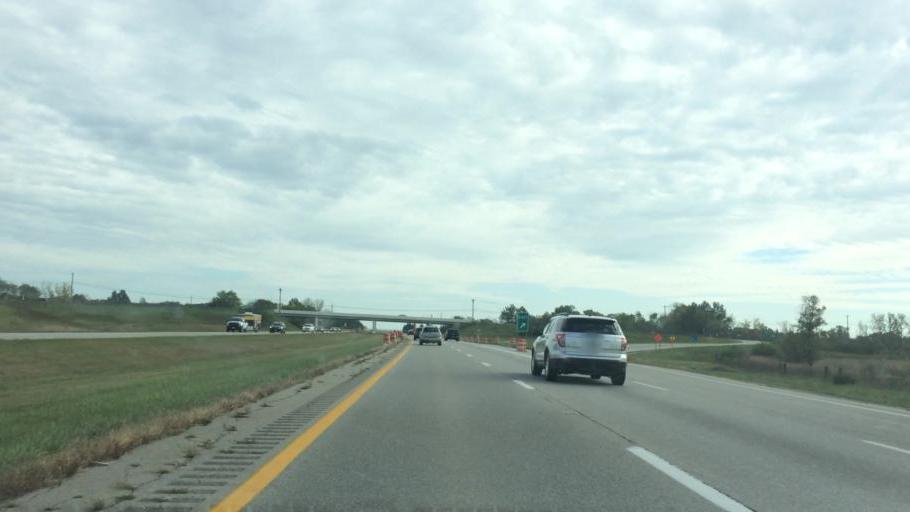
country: US
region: Ohio
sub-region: Union County
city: New California
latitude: 40.1632
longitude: -83.2344
